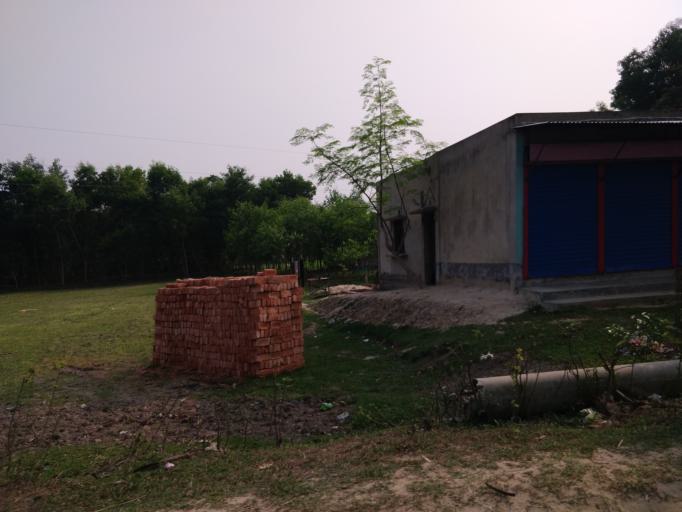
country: IN
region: Tripura
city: Khowai
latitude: 24.1298
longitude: 91.3689
